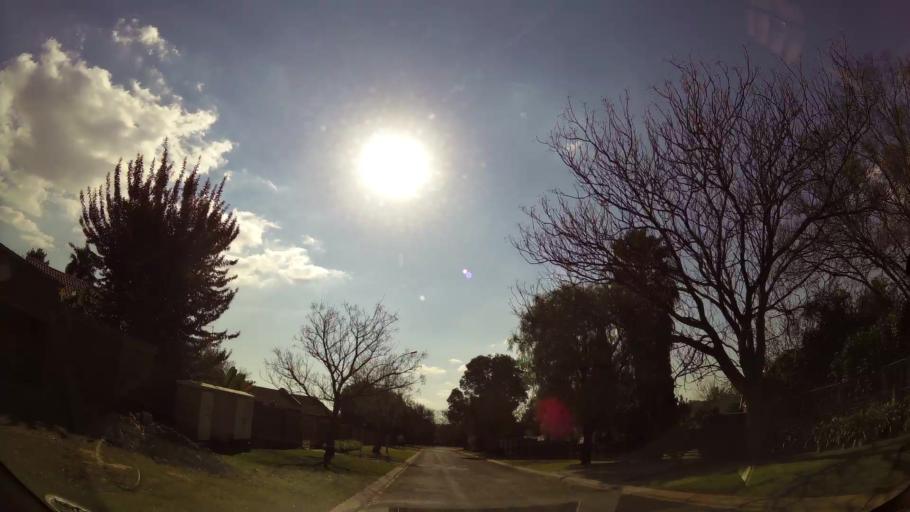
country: ZA
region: Gauteng
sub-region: Ekurhuleni Metropolitan Municipality
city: Benoni
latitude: -26.1405
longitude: 28.3513
